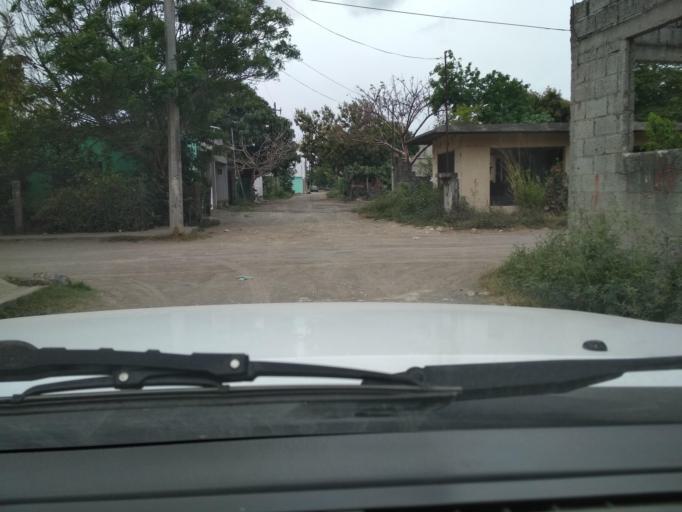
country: MX
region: Veracruz
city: Paso del Toro
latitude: 19.0616
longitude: -96.1327
